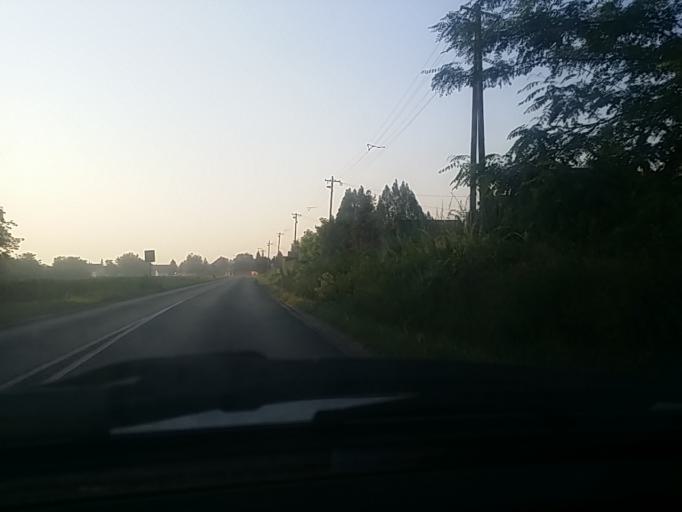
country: HU
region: Pest
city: Szentmartonkata
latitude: 47.4500
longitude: 19.6807
